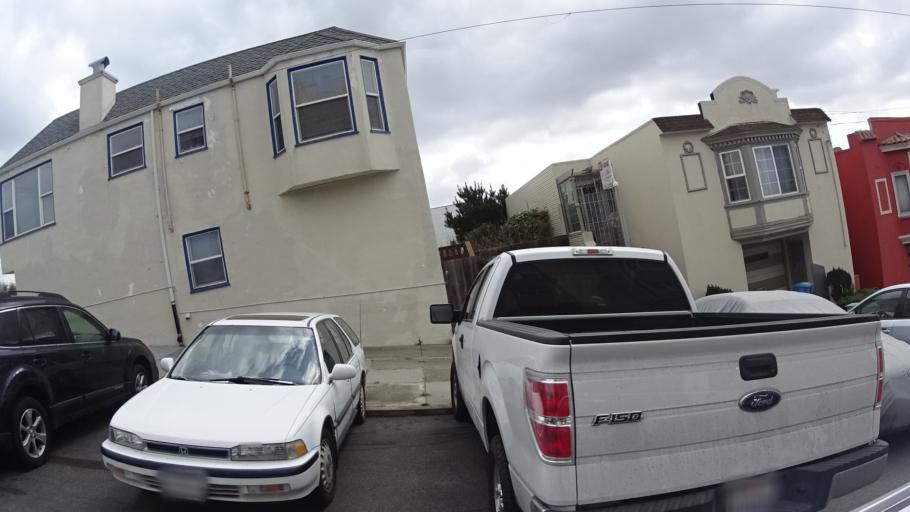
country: US
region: California
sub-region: San Mateo County
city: Daly City
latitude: 37.7769
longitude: -122.5060
